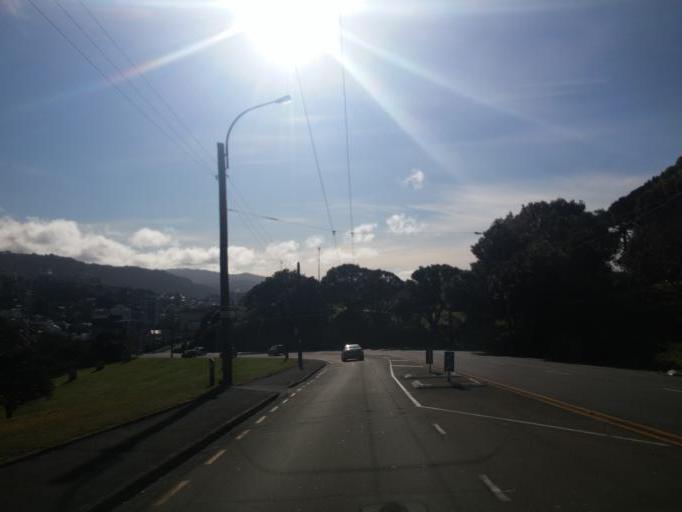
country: NZ
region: Wellington
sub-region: Wellington City
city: Wellington
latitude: -41.3029
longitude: 174.7695
